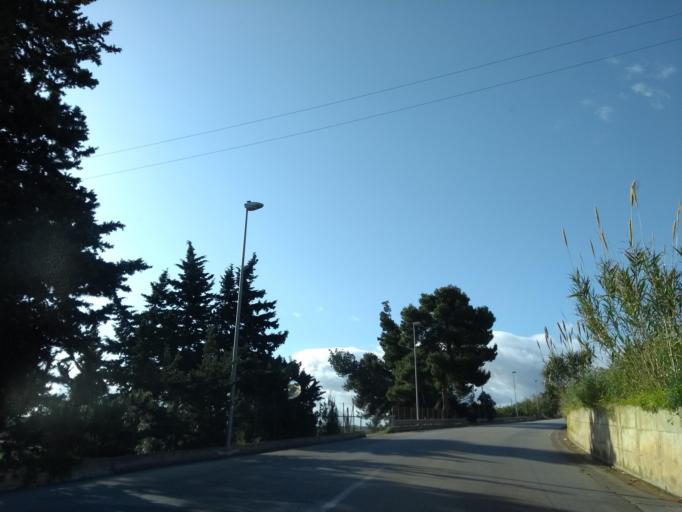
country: IT
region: Sicily
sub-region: Trapani
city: Alcamo
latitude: 38.0125
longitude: 12.9535
